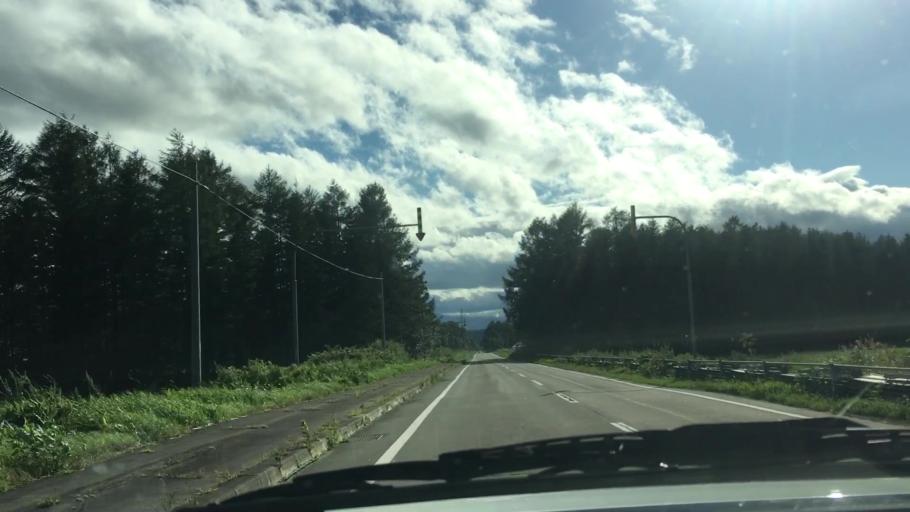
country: JP
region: Hokkaido
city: Otofuke
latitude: 43.1847
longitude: 143.0209
